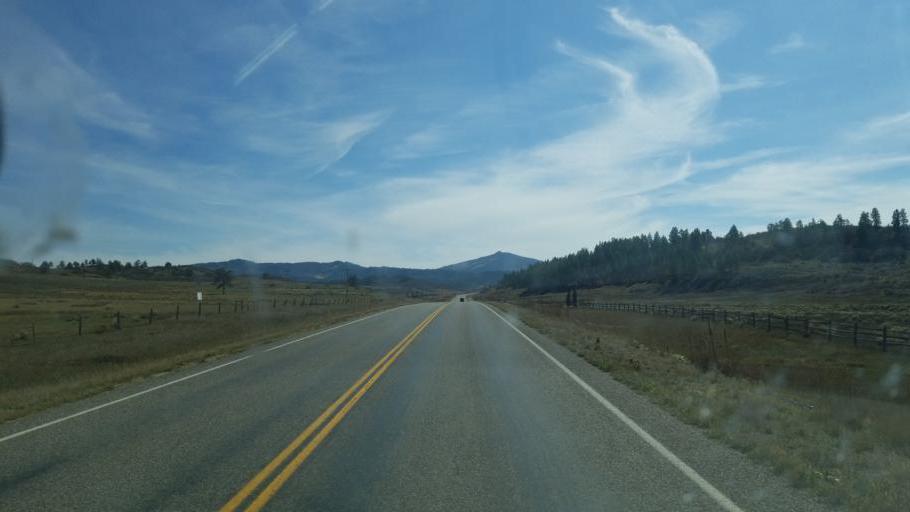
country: US
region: New Mexico
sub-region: Rio Arriba County
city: Dulce
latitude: 37.0212
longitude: -106.8166
